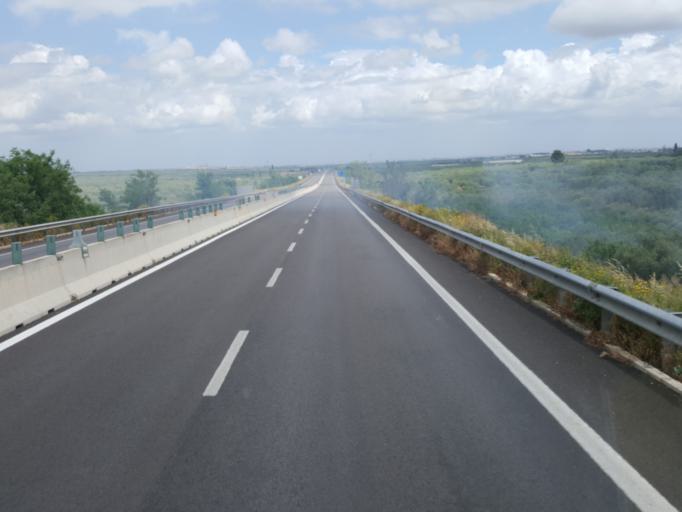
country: IT
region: Apulia
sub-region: Provincia di Bari
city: Toritto
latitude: 41.0008
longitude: 16.6674
